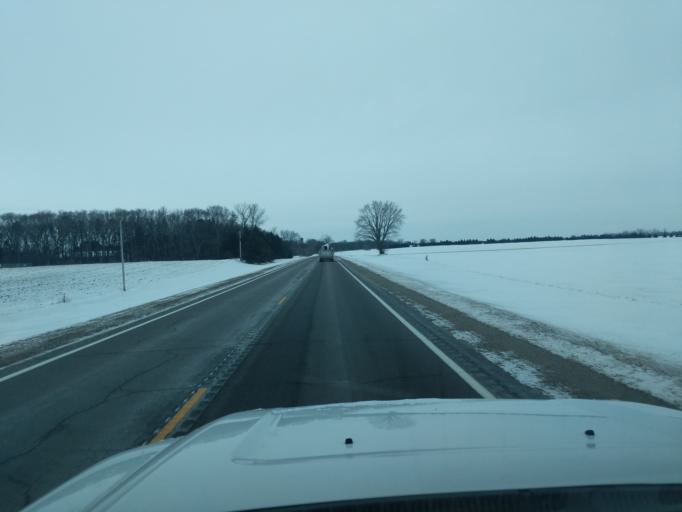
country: US
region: Minnesota
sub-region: Redwood County
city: Redwood Falls
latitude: 44.5743
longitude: -94.9946
